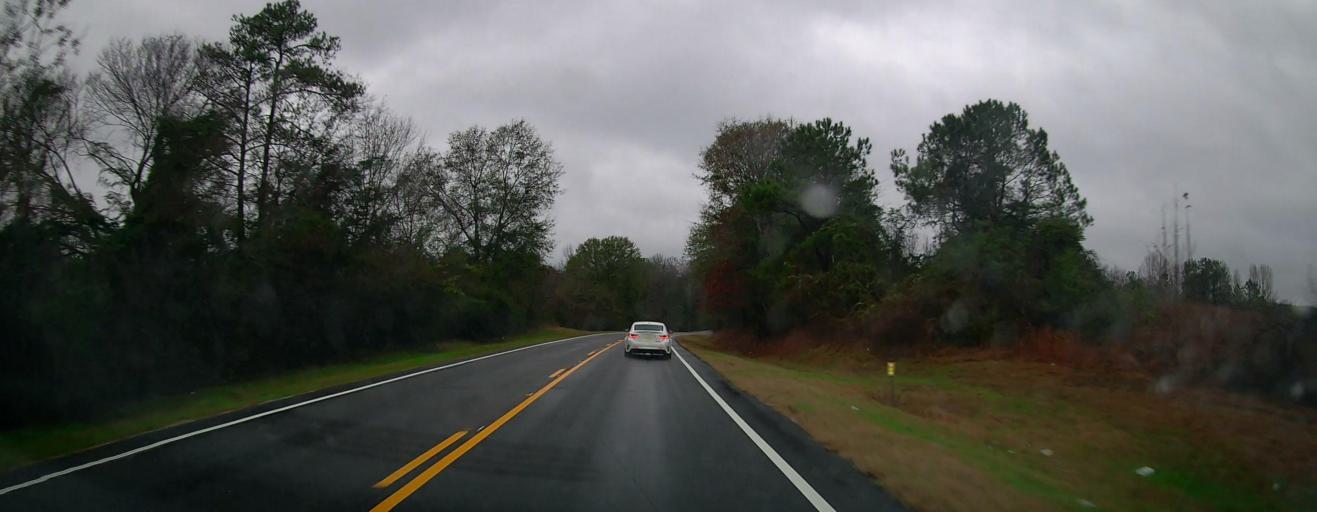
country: US
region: Alabama
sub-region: Chilton County
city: Clanton
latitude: 32.6709
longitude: -86.7837
